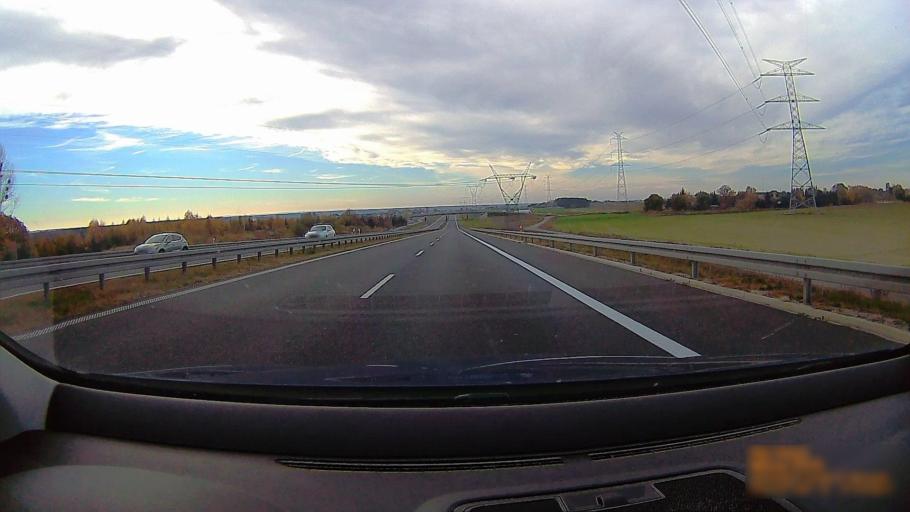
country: PL
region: Greater Poland Voivodeship
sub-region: Powiat ostrowski
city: Przygodzice
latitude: 51.6180
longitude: 17.8604
